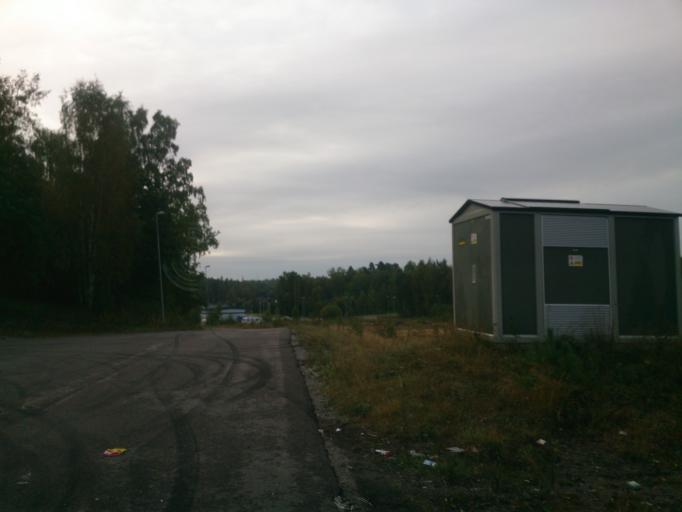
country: SE
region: OEstergoetland
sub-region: Atvidabergs Kommun
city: Atvidaberg
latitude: 58.2166
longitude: 15.9777
